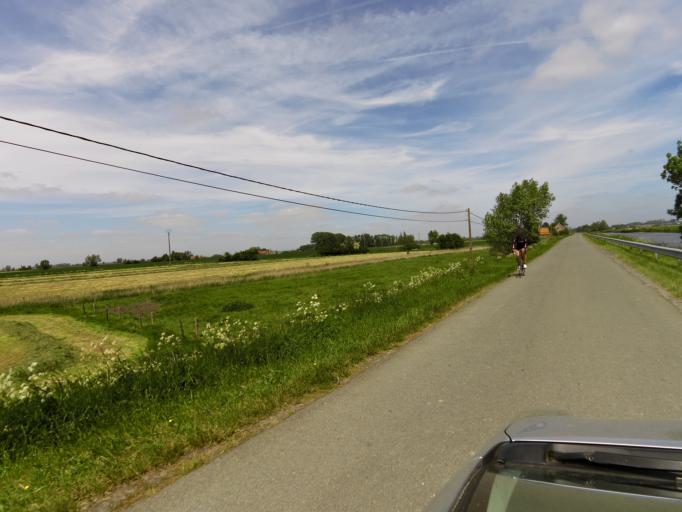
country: BE
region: Flanders
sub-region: Provincie West-Vlaanderen
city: Diksmuide
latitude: 51.0053
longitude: 2.8333
